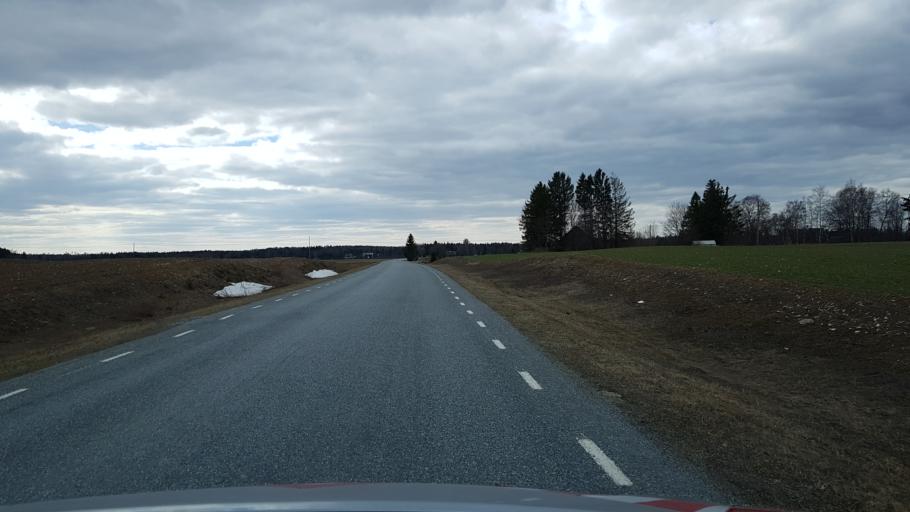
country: EE
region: Laeaene-Virumaa
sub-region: Rakvere linn
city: Rakvere
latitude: 59.2644
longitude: 26.2590
